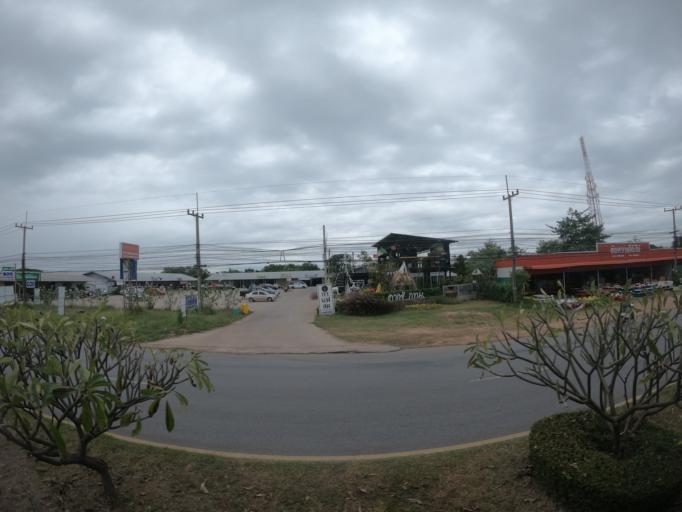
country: TH
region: Maha Sarakham
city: Maha Sarakham
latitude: 16.1746
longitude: 103.2951
